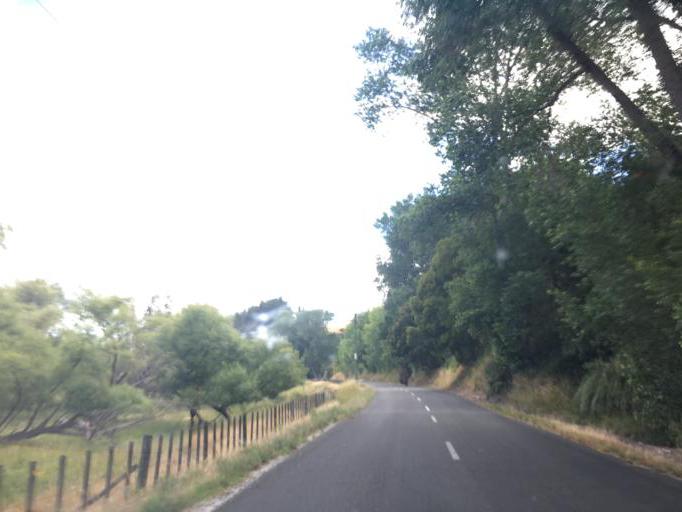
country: NZ
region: Hawke's Bay
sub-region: Hastings District
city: Hastings
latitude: -39.7291
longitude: 176.9176
